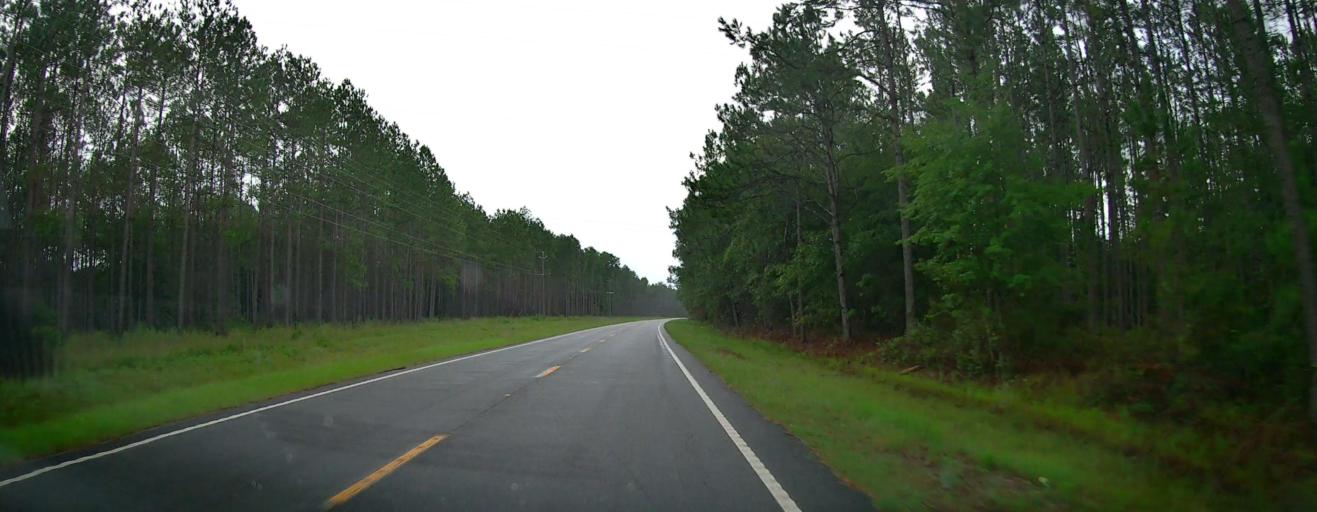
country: US
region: Georgia
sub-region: Ware County
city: Deenwood
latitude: 31.2696
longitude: -82.5237
